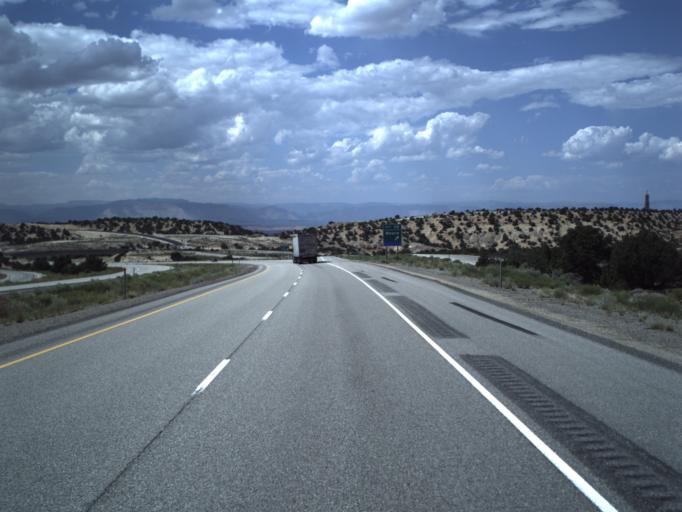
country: US
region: Utah
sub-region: Emery County
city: Ferron
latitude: 38.8531
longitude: -110.9083
